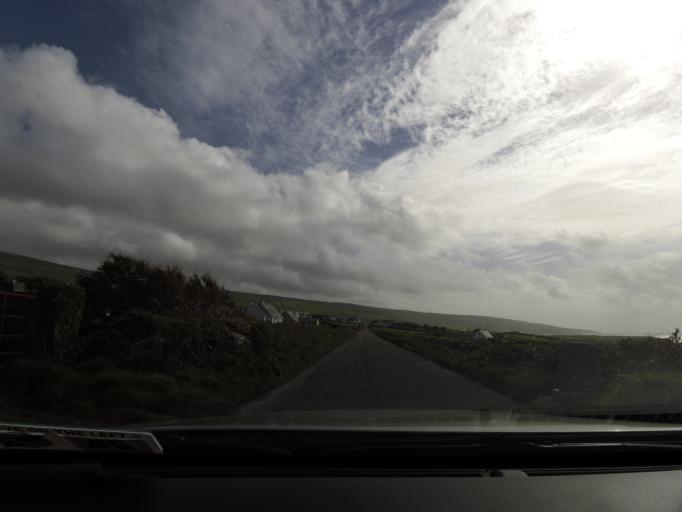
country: IE
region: Connaught
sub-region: County Galway
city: Bearna
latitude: 53.1052
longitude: -9.2954
